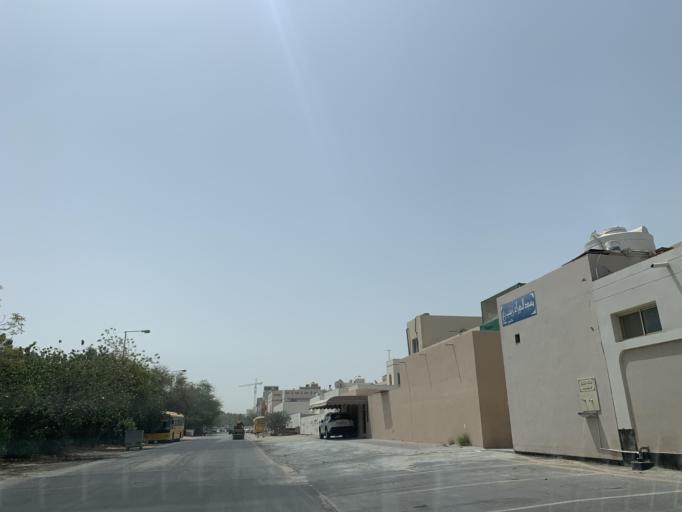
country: BH
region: Northern
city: Madinat `Isa
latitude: 26.1640
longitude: 50.5277
